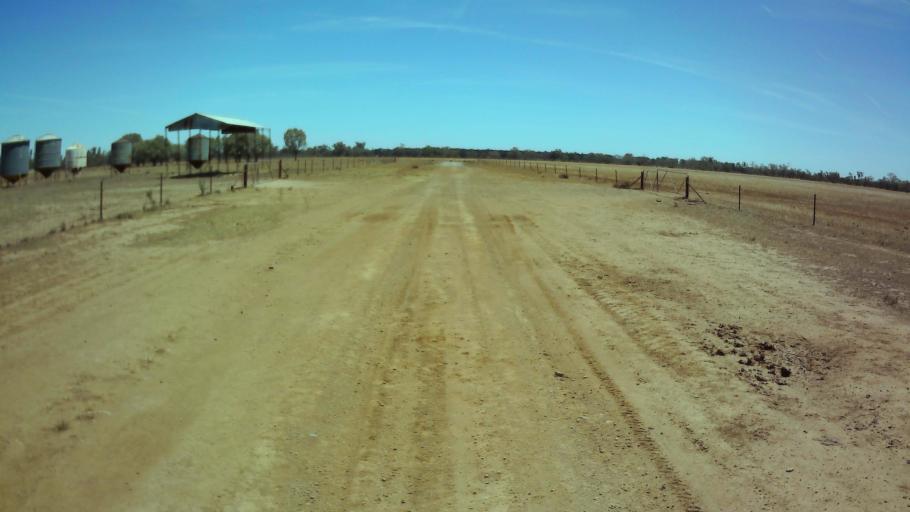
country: AU
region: New South Wales
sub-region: Bland
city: West Wyalong
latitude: -33.8275
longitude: 147.6386
